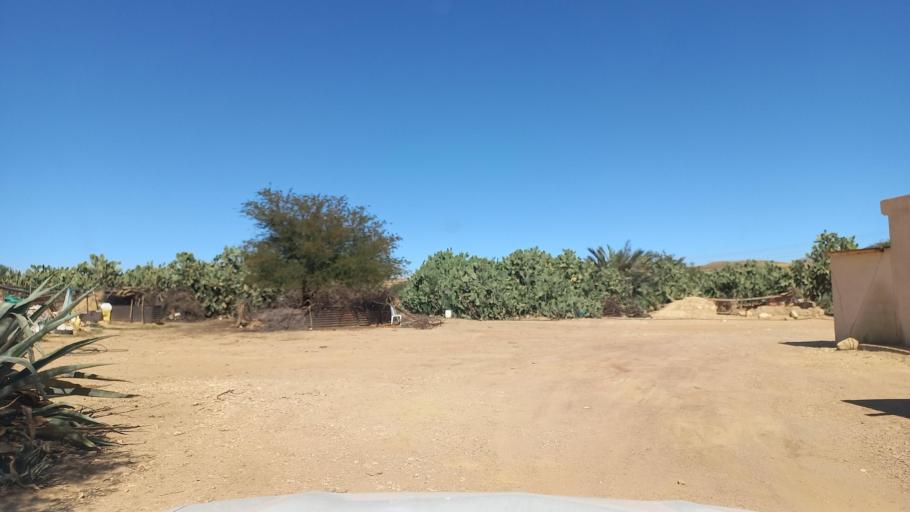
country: TN
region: Al Qasrayn
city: Sbiba
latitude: 35.3630
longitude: 9.0918
